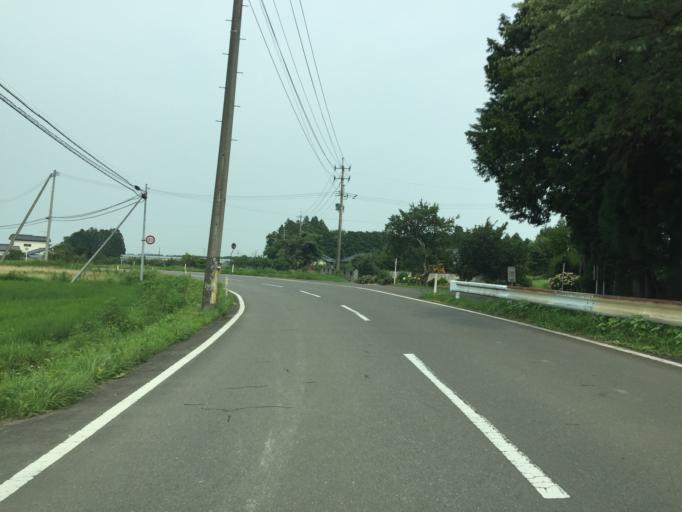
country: JP
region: Fukushima
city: Namie
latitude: 37.6003
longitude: 140.9182
